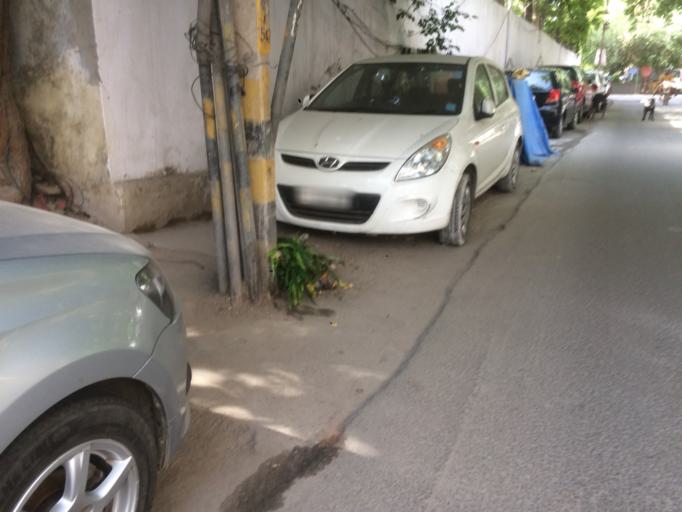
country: IN
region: Uttar Pradesh
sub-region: Gautam Buddha Nagar
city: Noida
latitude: 28.5601
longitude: 77.2574
